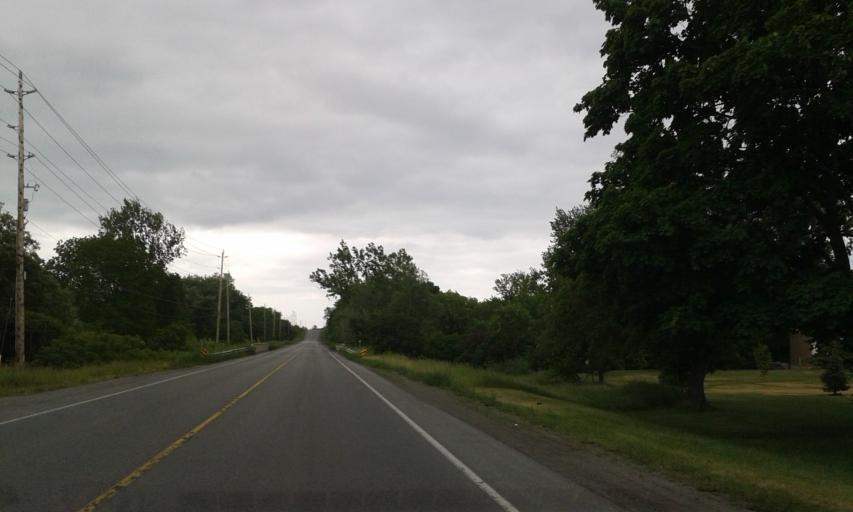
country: CA
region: Ontario
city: Quinte West
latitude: 43.9975
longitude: -77.5185
